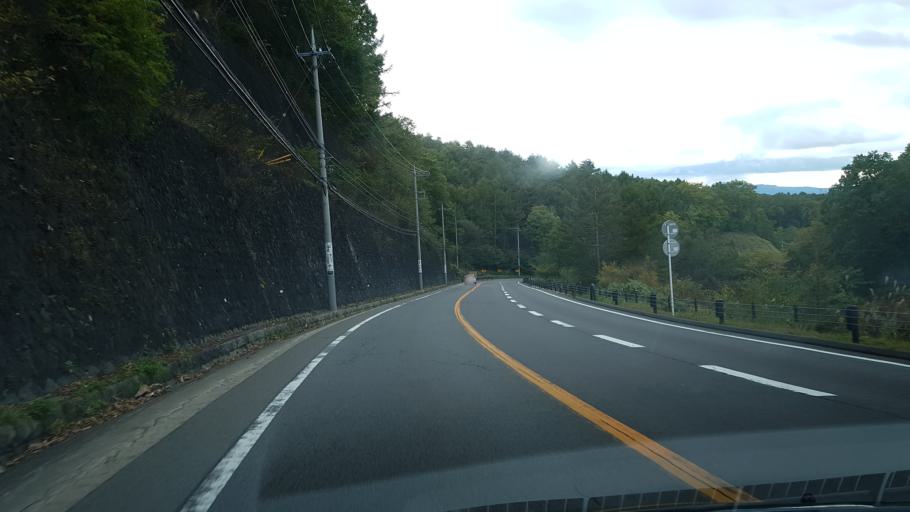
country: JP
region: Gunma
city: Nakanojomachi
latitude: 36.6015
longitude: 138.5861
